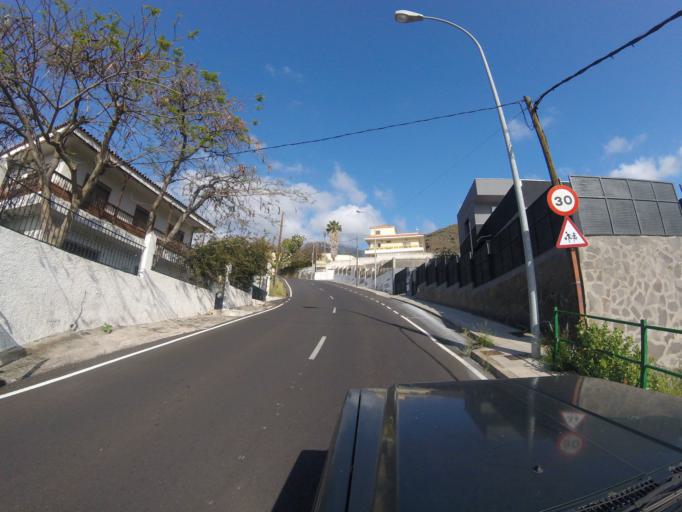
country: ES
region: Canary Islands
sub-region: Provincia de Santa Cruz de Tenerife
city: Candelaria
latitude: 28.3827
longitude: -16.3676
